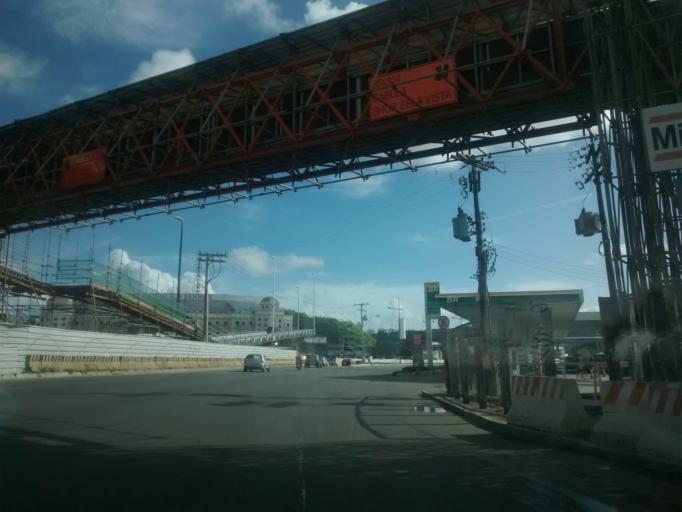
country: BR
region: Bahia
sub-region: Salvador
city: Salvador
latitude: -12.9787
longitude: -38.4643
